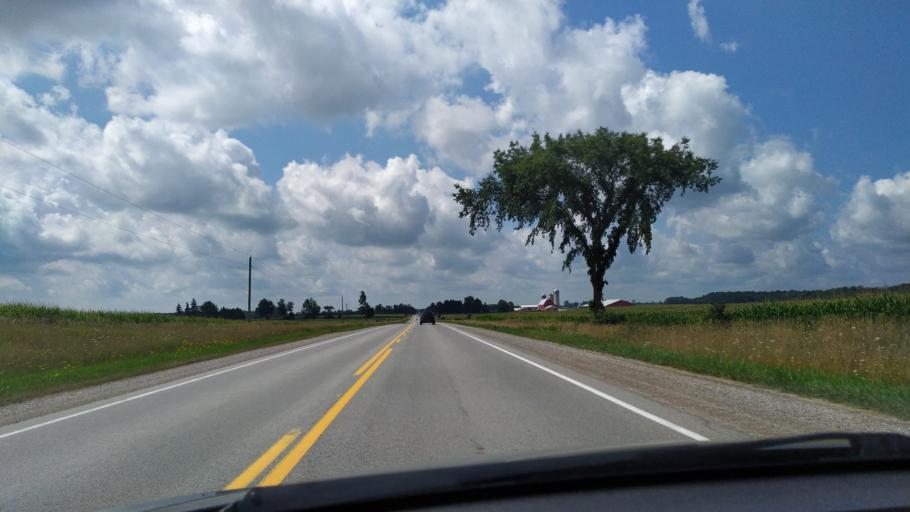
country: CA
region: Ontario
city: South Huron
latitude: 43.2966
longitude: -81.3364
